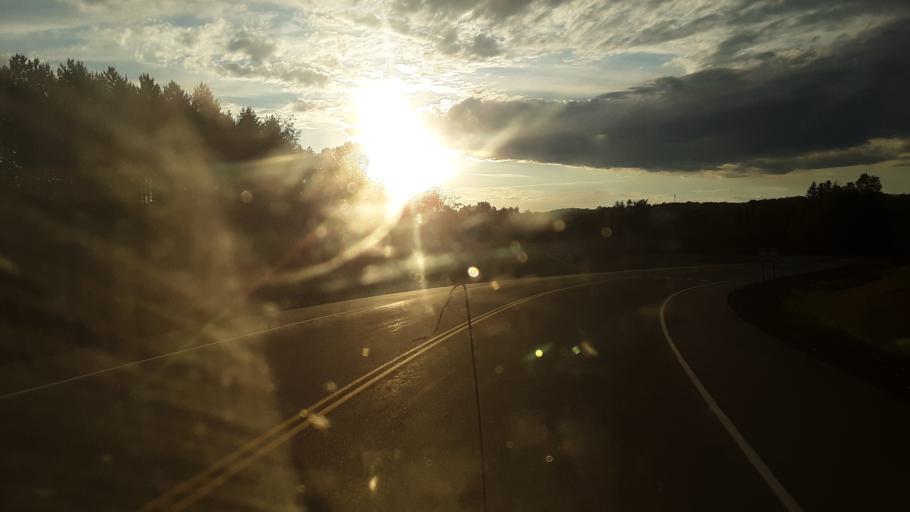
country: US
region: Maine
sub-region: Aroostook County
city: Presque Isle
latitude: 46.6934
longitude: -67.9811
